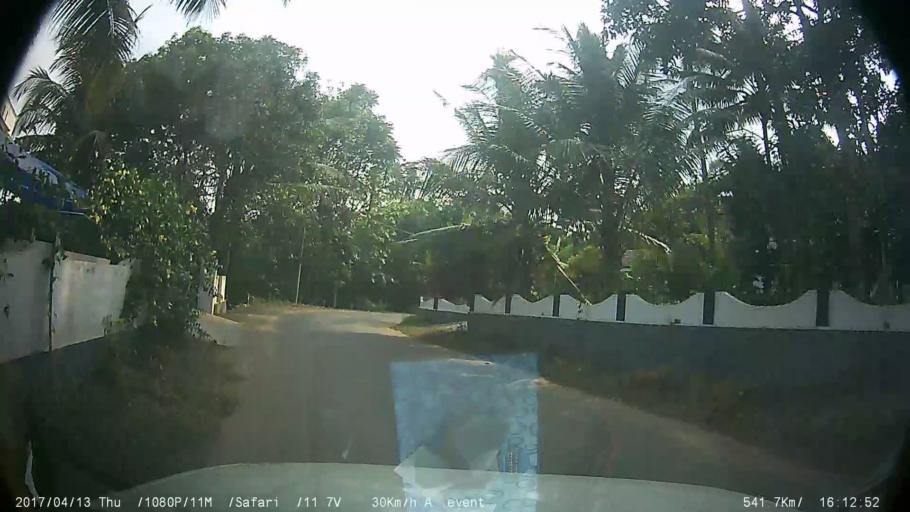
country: IN
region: Kerala
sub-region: Ernakulam
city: Piravam
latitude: 9.8204
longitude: 76.5153
